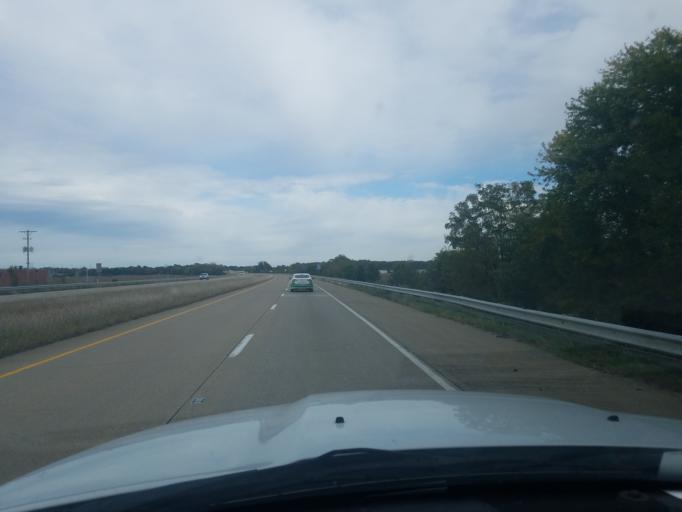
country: US
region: Indiana
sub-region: Vanderburgh County
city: Evansville
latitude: 37.9413
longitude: -87.4843
